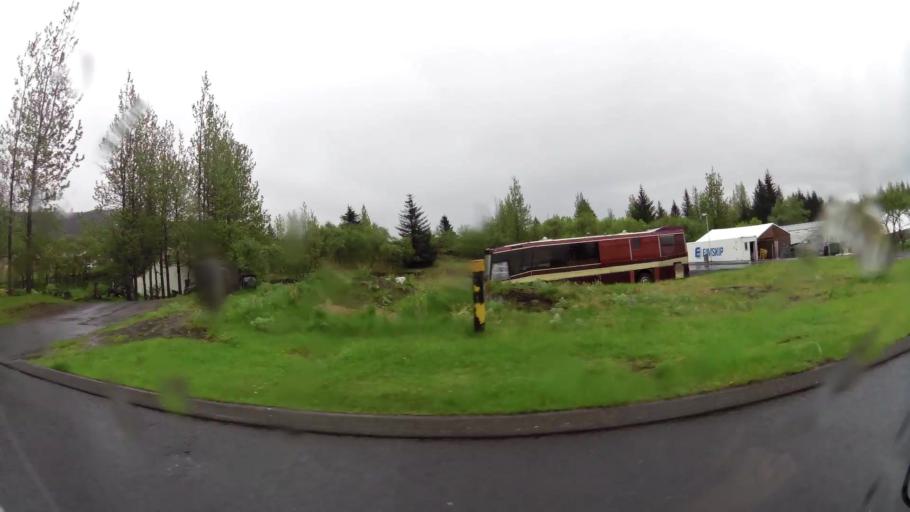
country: IS
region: South
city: Hveragerdi
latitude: 64.0045
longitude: -21.1904
